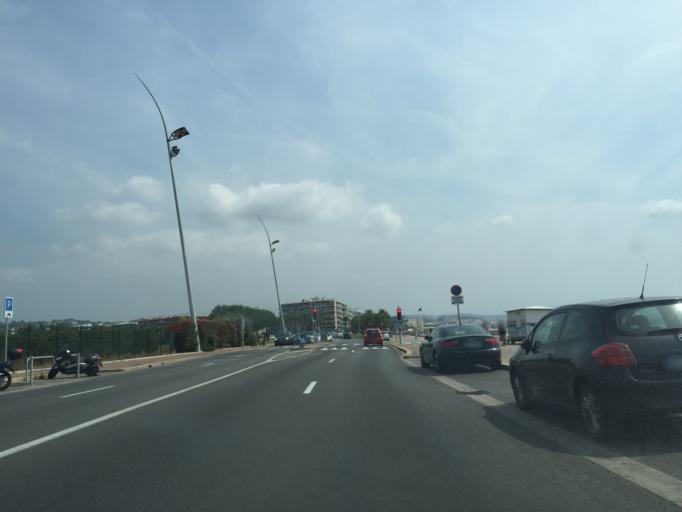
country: FR
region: Provence-Alpes-Cote d'Azur
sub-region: Departement des Alpes-Maritimes
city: Cagnes-sur-Mer
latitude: 43.6487
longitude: 7.1497
